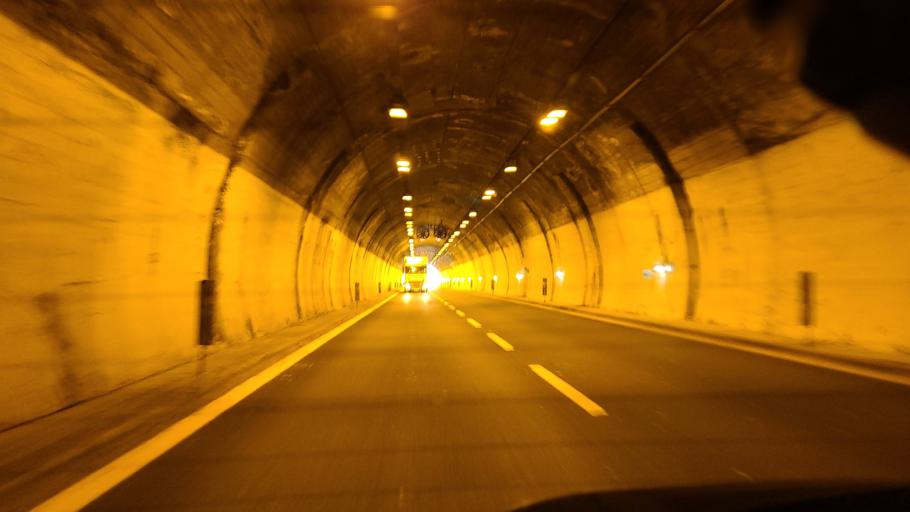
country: IT
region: Liguria
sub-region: Provincia di Imperia
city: Ventimiglia
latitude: 43.7991
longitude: 7.5884
